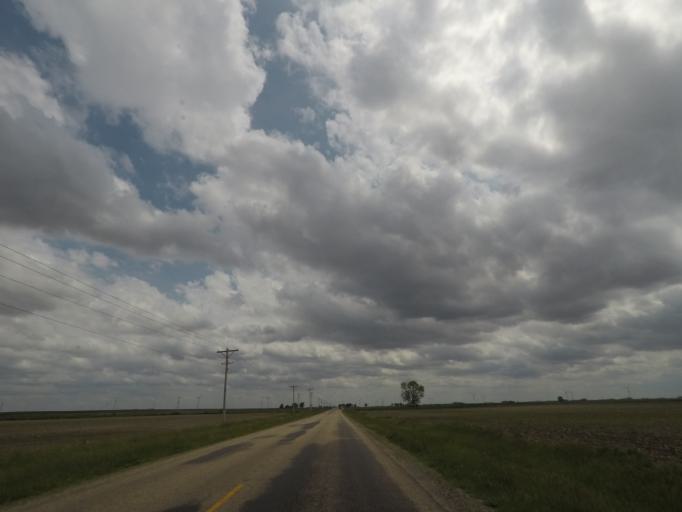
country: US
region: Illinois
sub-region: Macon County
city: Maroa
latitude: 40.0736
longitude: -89.0860
